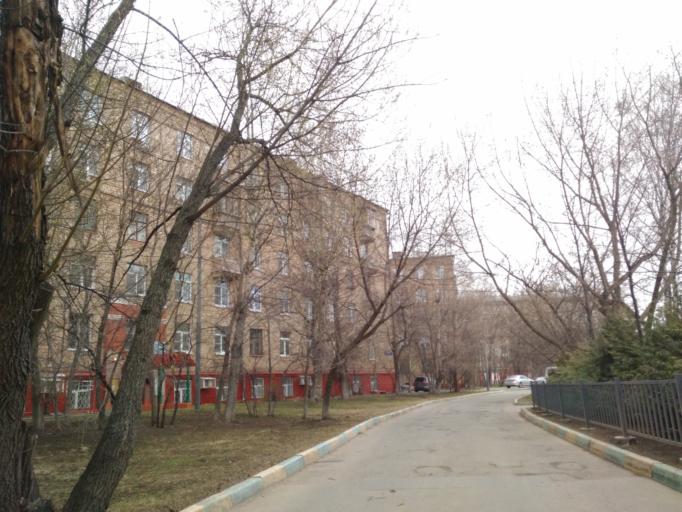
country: RU
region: Moskovskaya
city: Khoroshevo-Mnevniki
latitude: 55.7890
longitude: 37.4766
